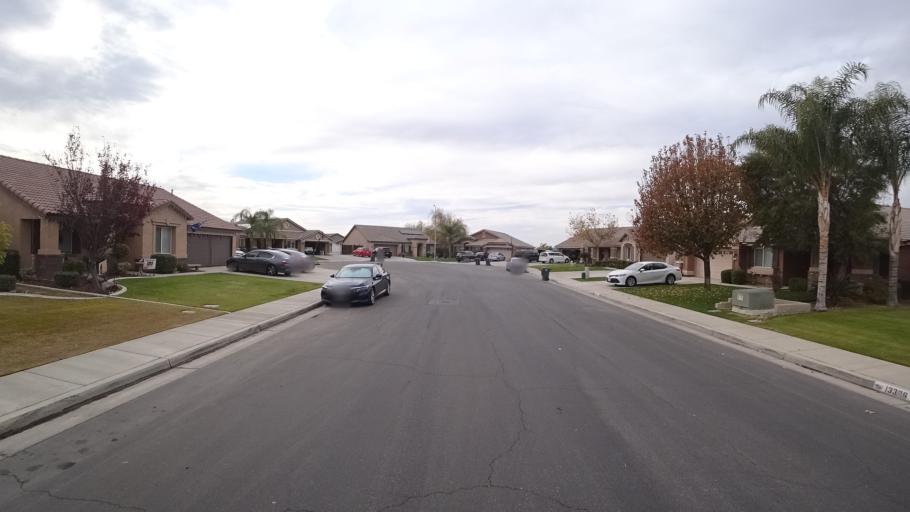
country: US
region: California
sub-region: Kern County
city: Rosedale
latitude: 35.4094
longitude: -119.1494
